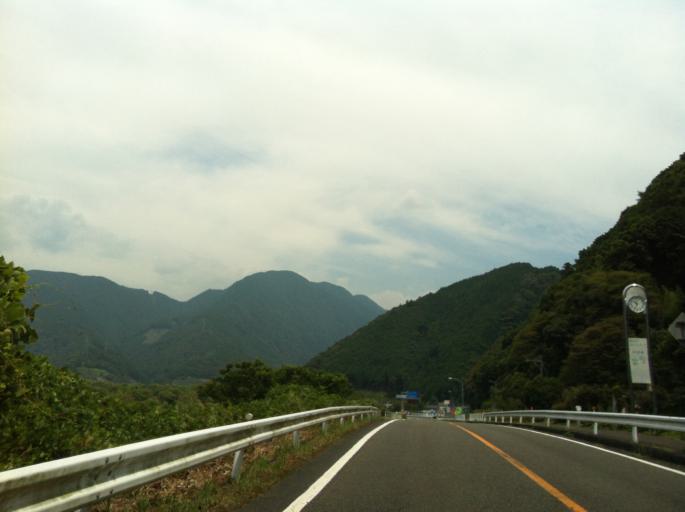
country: JP
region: Shizuoka
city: Shizuoka-shi
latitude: 35.1035
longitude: 138.3667
